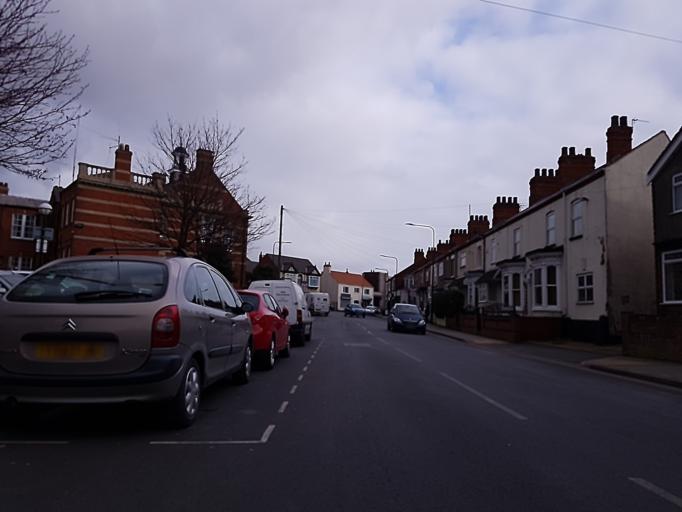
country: GB
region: England
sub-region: North East Lincolnshire
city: Cleethorpes
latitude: 53.5576
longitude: -0.0285
